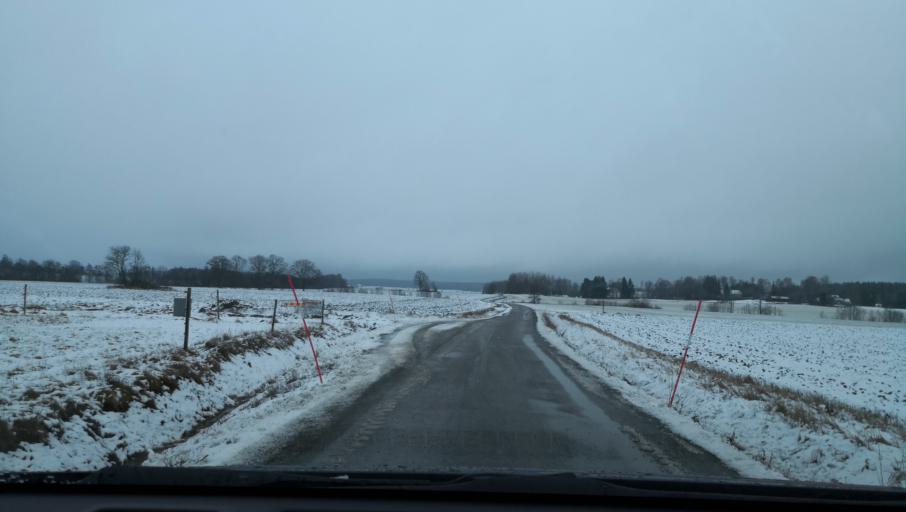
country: SE
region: Vaestmanland
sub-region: Kopings Kommun
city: Kolsva
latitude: 59.5414
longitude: 15.8816
